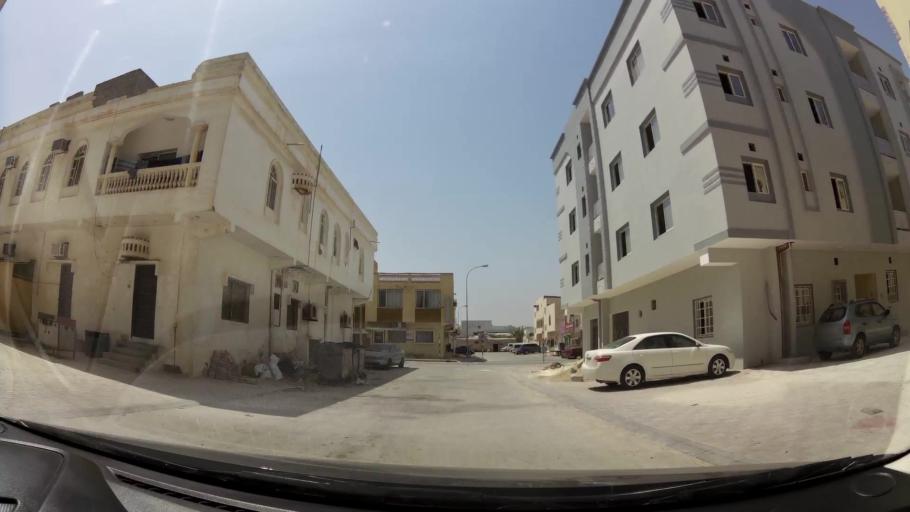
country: OM
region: Zufar
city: Salalah
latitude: 17.0144
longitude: 54.0863
